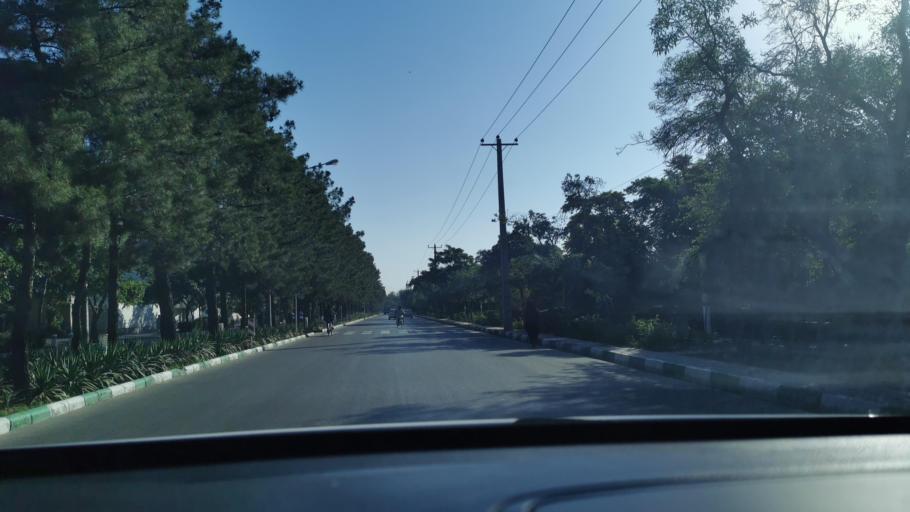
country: IR
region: Razavi Khorasan
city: Mashhad
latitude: 36.3125
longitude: 59.5229
